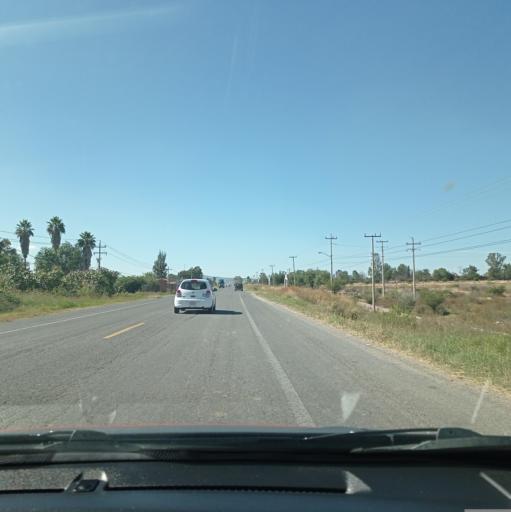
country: MX
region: Jalisco
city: San Miguel el Alto
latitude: 21.0190
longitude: -102.3429
